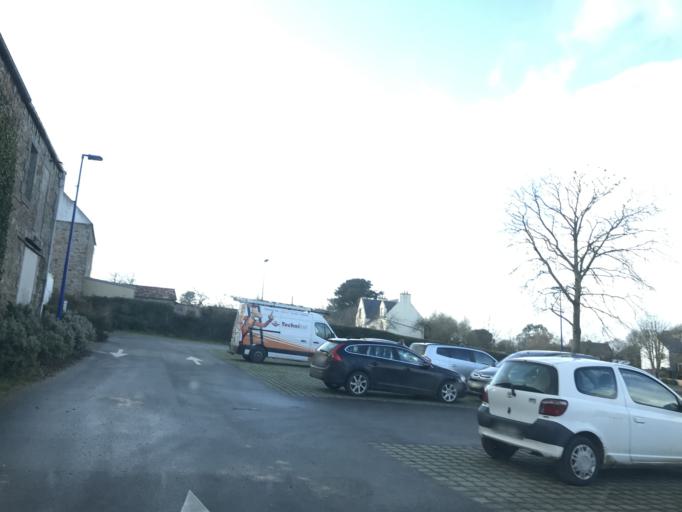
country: FR
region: Brittany
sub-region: Departement du Finistere
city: Lanmeur
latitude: 48.6477
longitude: -3.7169
